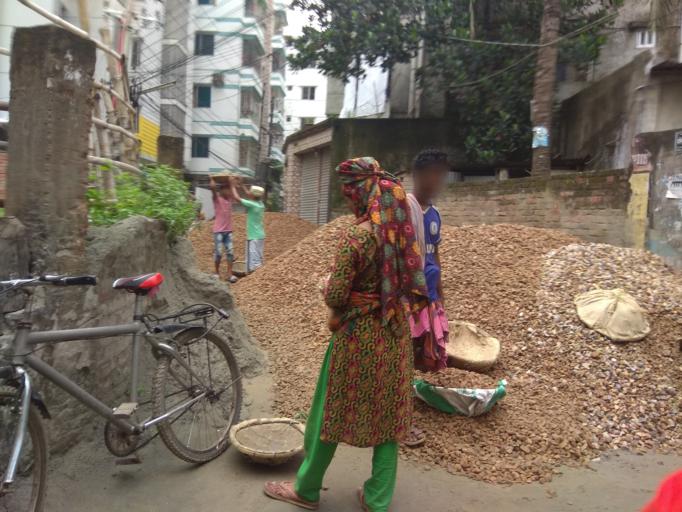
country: BD
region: Dhaka
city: Azimpur
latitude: 23.7947
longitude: 90.3687
